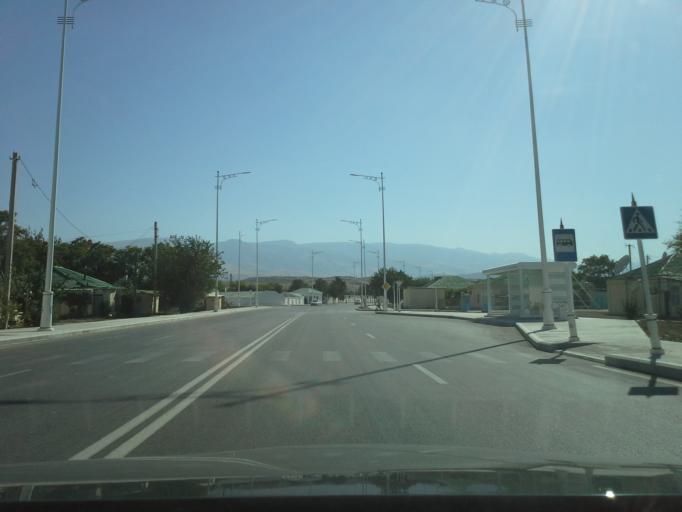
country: TM
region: Ahal
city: Ashgabat
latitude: 37.9659
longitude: 58.3462
